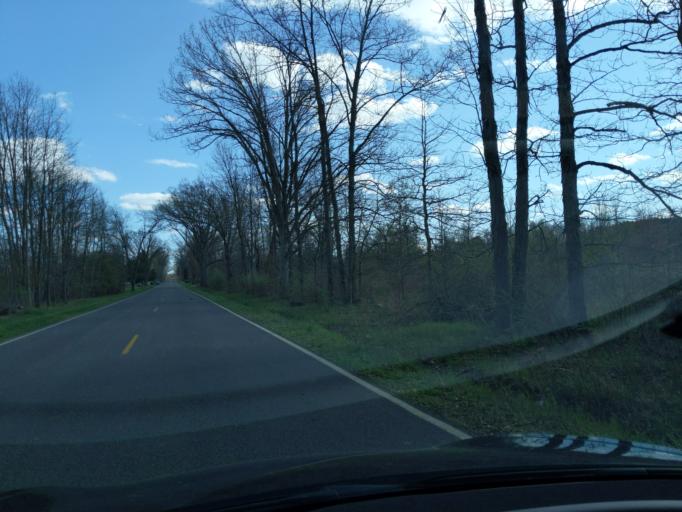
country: US
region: Michigan
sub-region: Ingham County
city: Leslie
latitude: 42.3860
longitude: -84.5416
